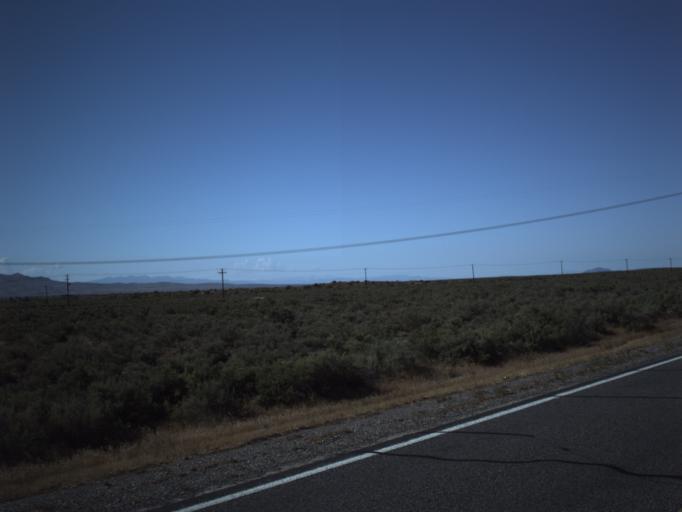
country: US
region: Utah
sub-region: Millard County
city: Delta
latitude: 39.4905
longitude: -112.4028
